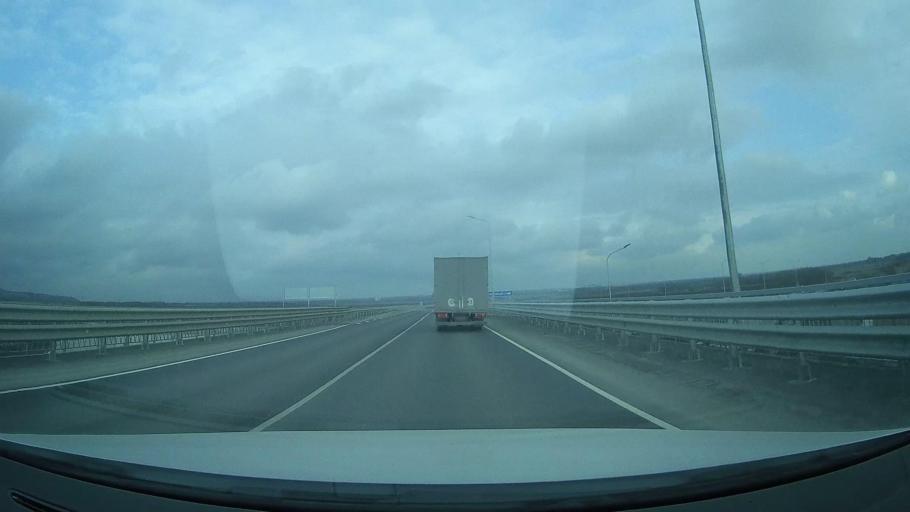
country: RU
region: Rostov
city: Grushevskaya
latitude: 47.4541
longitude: 39.8833
